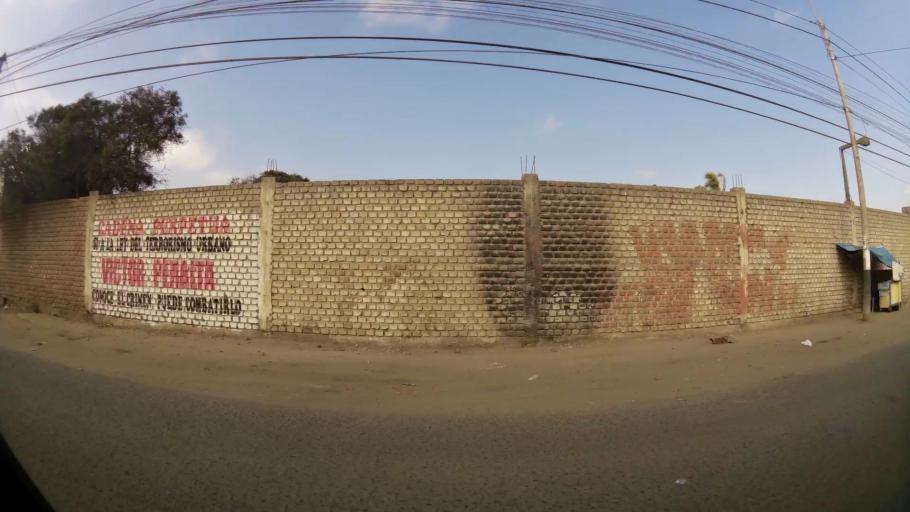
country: PE
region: La Libertad
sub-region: Provincia de Trujillo
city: El Porvenir
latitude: -8.1067
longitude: -79.0038
